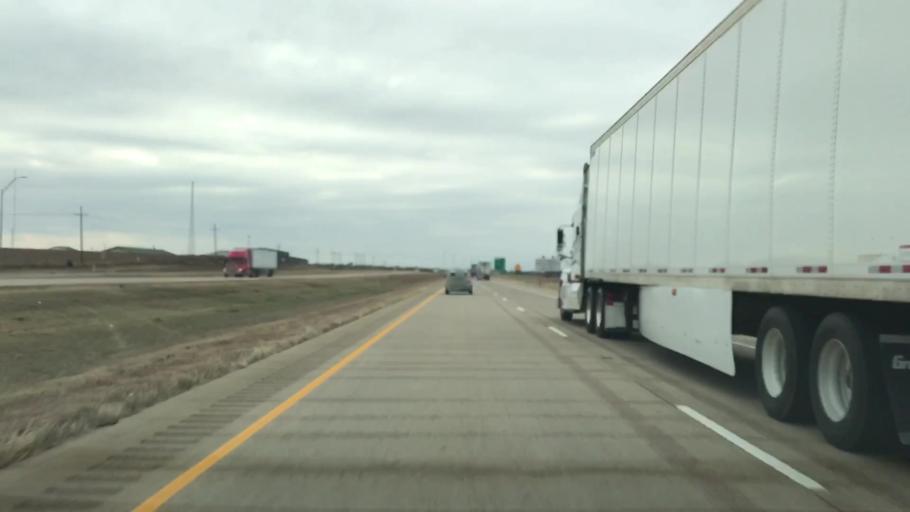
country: US
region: Texas
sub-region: Wheeler County
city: Shamrock
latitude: 35.2270
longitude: -100.2132
